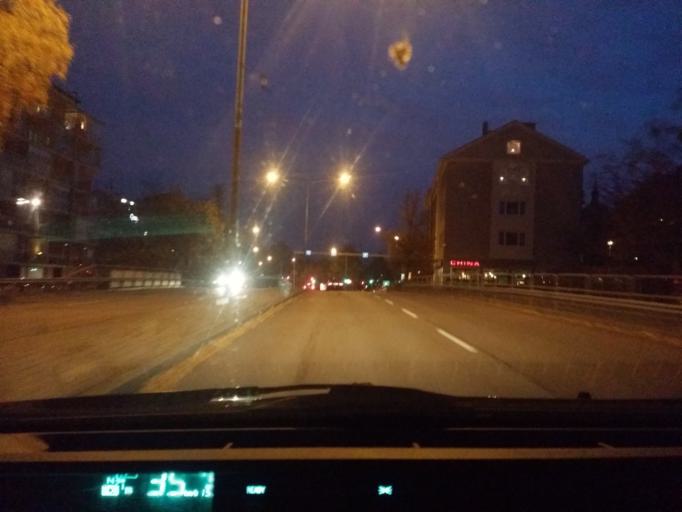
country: SE
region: Vaestmanland
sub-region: Vasteras
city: Vasteras
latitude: 59.6093
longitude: 16.5373
